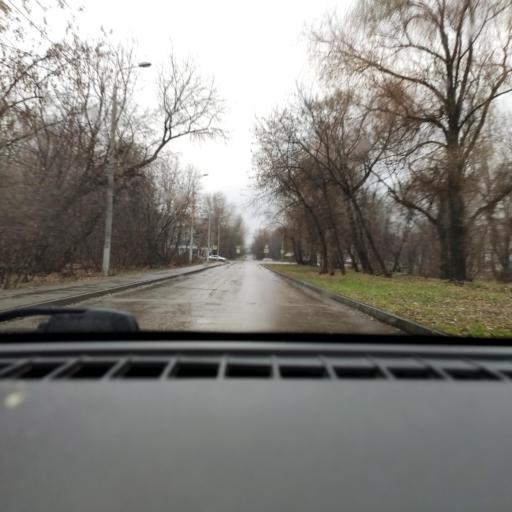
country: RU
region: Perm
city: Kultayevo
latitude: 57.9967
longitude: 55.9346
